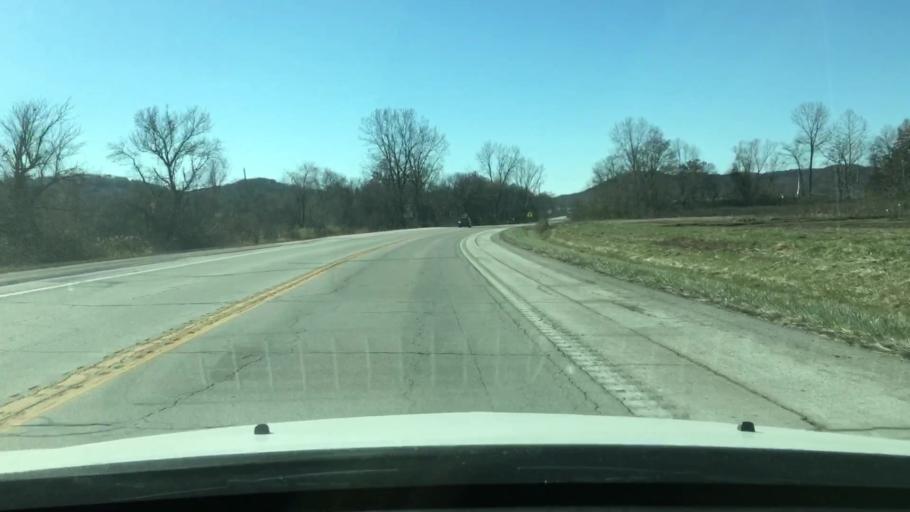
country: US
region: Missouri
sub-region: Pike County
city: Louisiana
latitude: 39.4198
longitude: -91.0885
